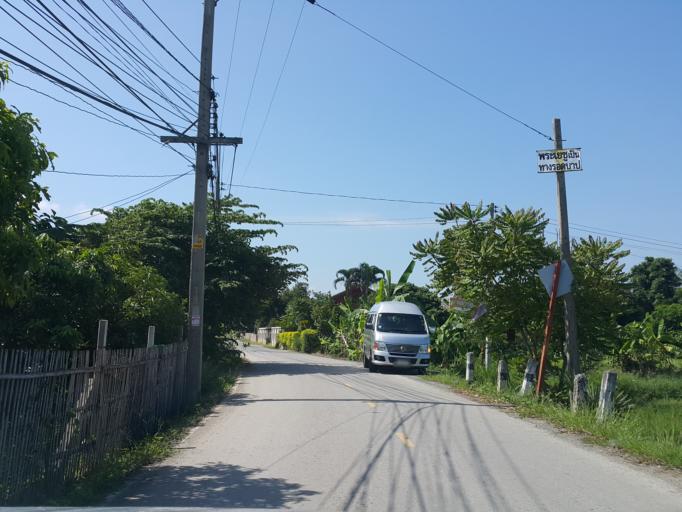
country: TH
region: Chiang Mai
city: San Kamphaeng
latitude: 18.7455
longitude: 99.1688
